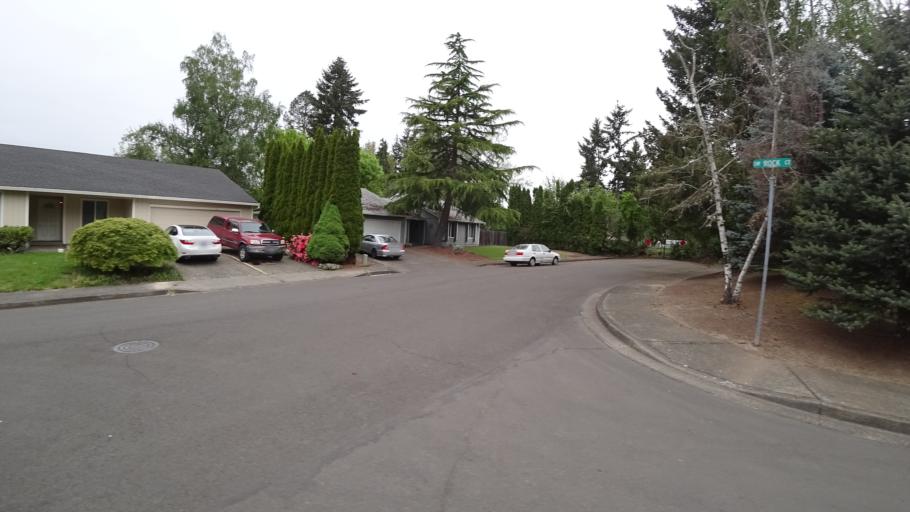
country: US
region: Oregon
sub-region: Washington County
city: Aloha
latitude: 45.5069
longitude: -122.8740
